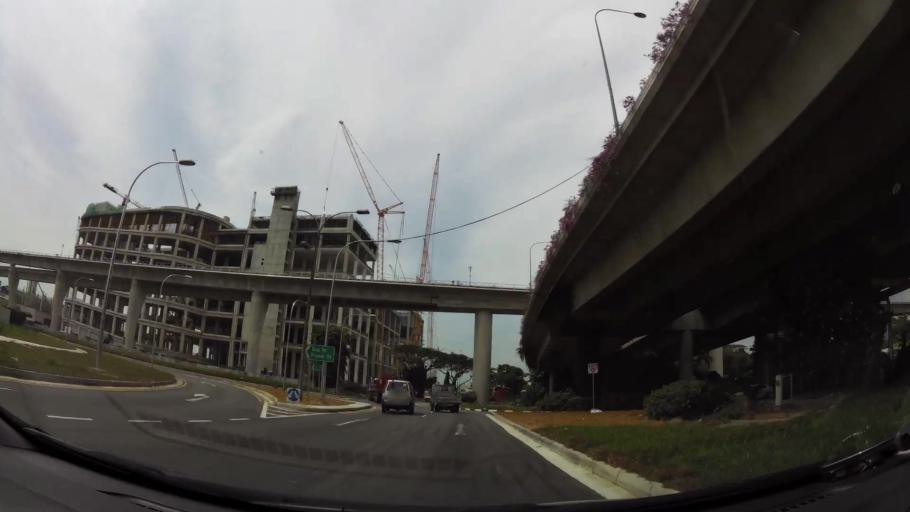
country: MY
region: Johor
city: Johor Bahru
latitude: 1.3222
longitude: 103.6638
